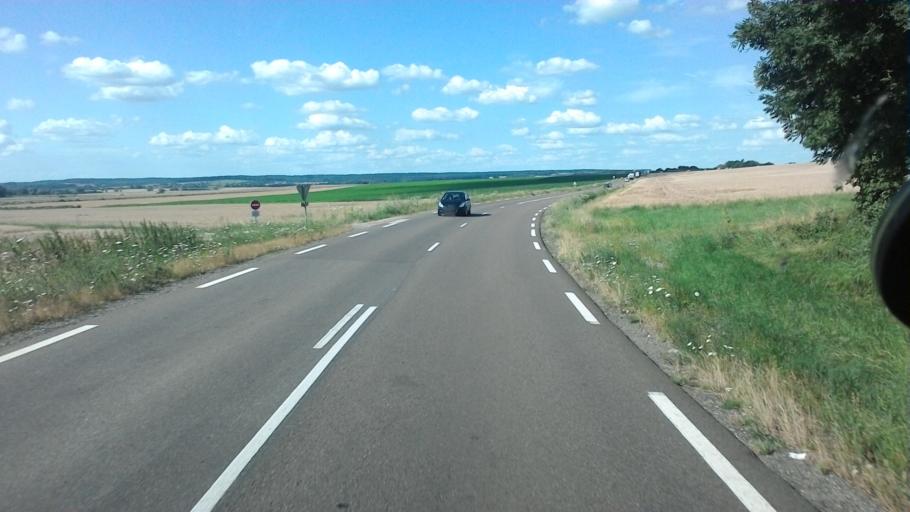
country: FR
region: Franche-Comte
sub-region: Departement de la Haute-Saone
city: Gy
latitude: 47.3925
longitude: 5.7909
